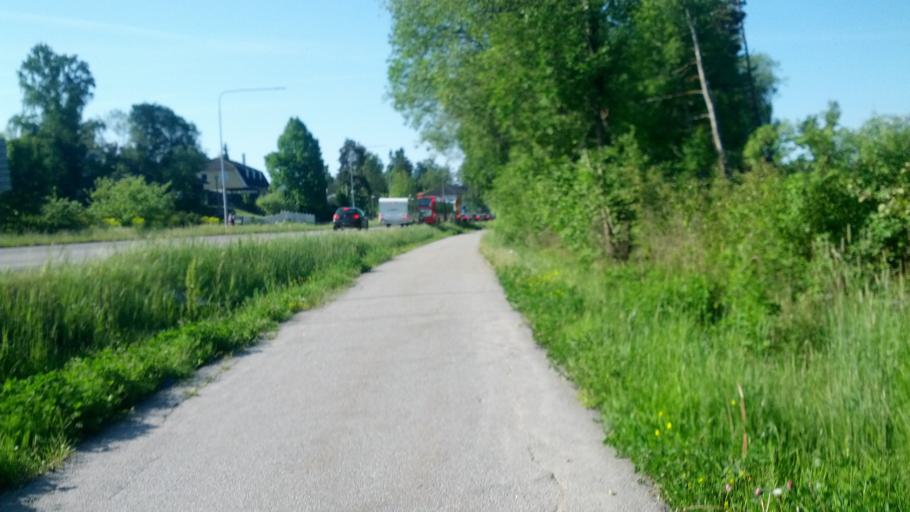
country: SE
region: Stockholm
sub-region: Taby Kommun
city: Taby
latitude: 59.4537
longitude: 18.0362
